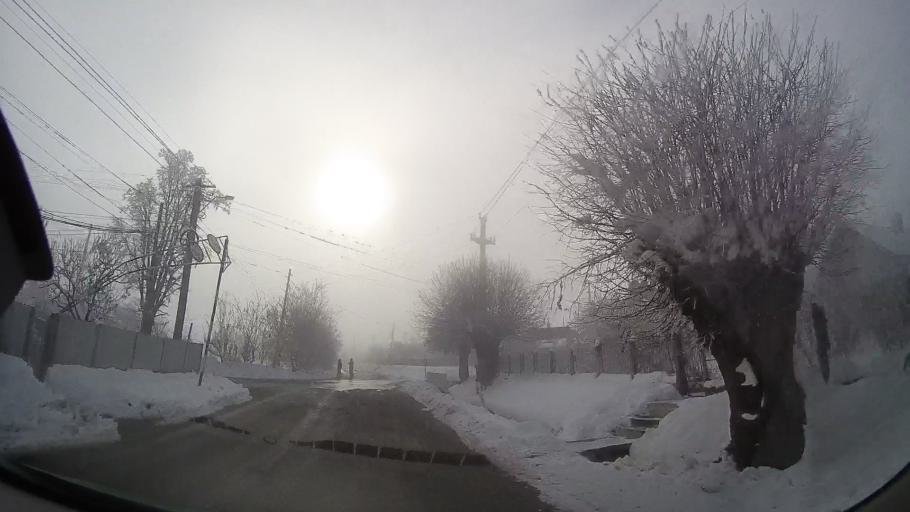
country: RO
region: Iasi
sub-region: Comuna Valea Seaca
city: Topile
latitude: 47.2567
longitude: 26.6661
